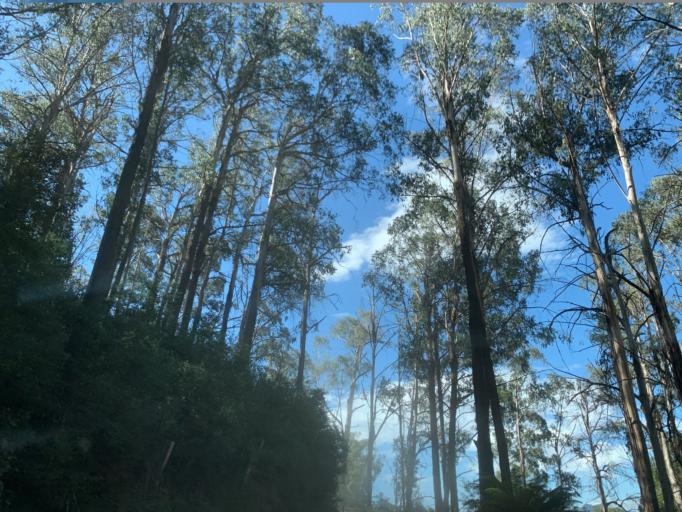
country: AU
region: Victoria
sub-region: Mansfield
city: Mansfield
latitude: -37.1019
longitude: 146.4989
